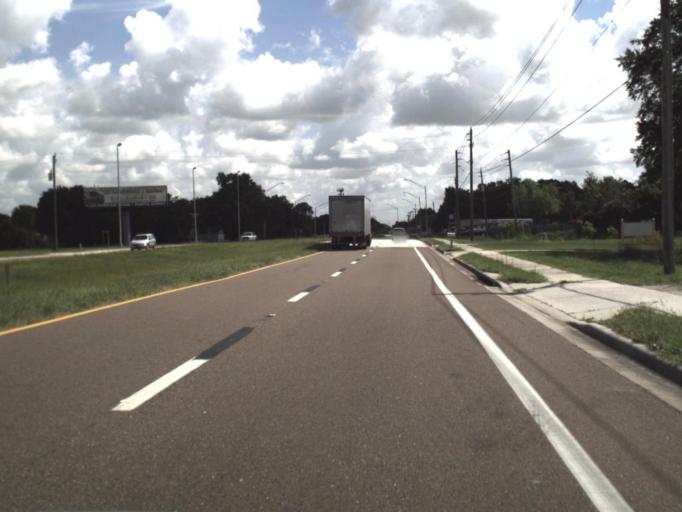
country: US
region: Florida
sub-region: Charlotte County
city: Cleveland
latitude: 26.9683
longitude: -81.9665
